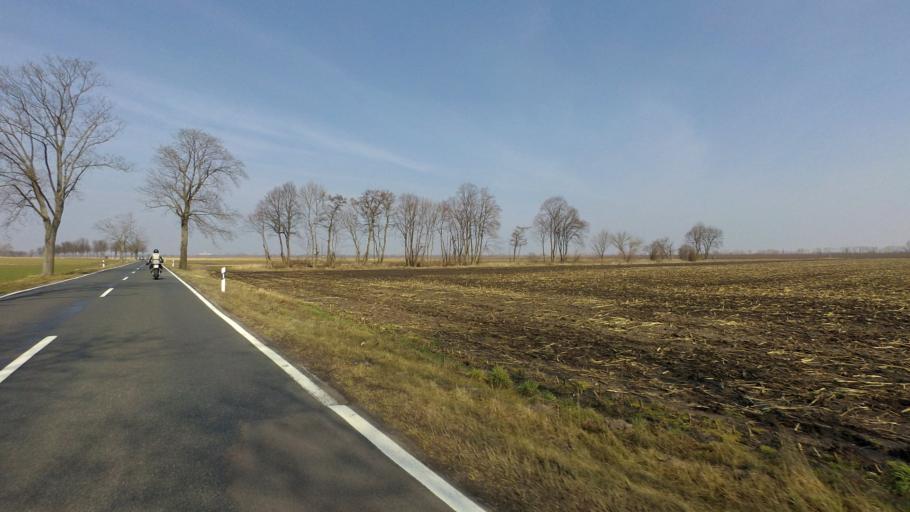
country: DE
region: Brandenburg
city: Ketzin
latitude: 52.4391
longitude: 12.8575
